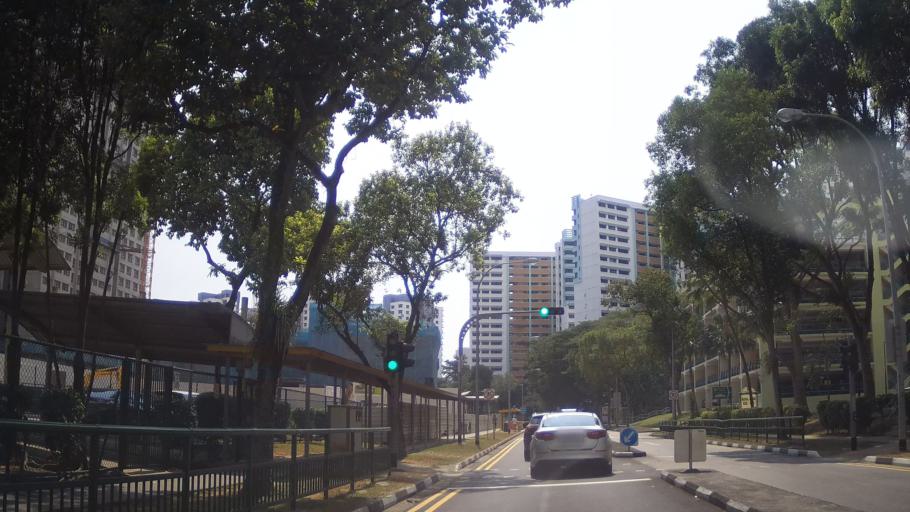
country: MY
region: Johor
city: Johor Bahru
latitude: 1.3870
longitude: 103.7601
